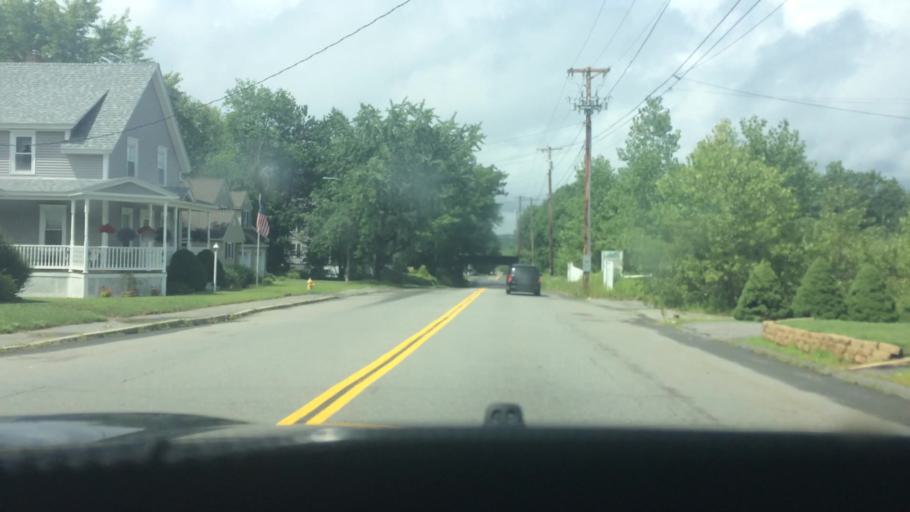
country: US
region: Massachusetts
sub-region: Worcester County
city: Gardner
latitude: 42.5744
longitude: -72.0108
